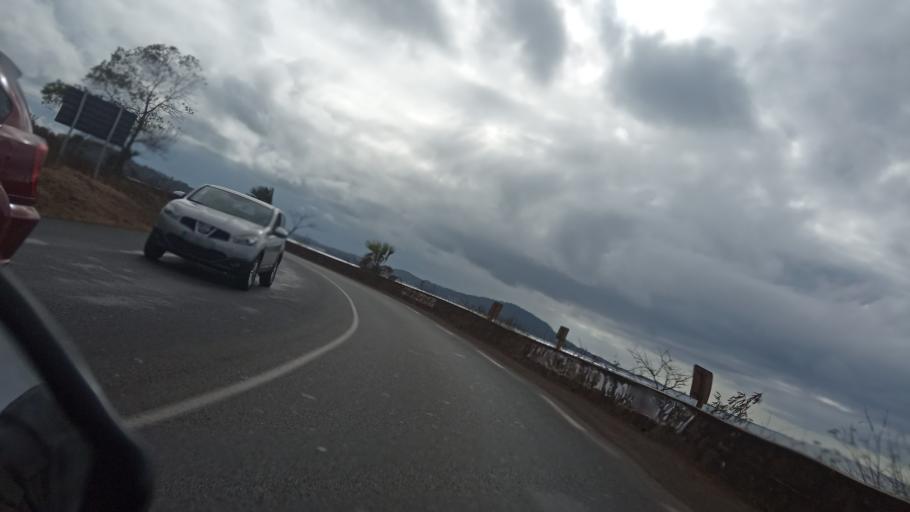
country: YT
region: Mamoudzou
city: Mamoudzou
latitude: -12.7946
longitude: 45.2178
